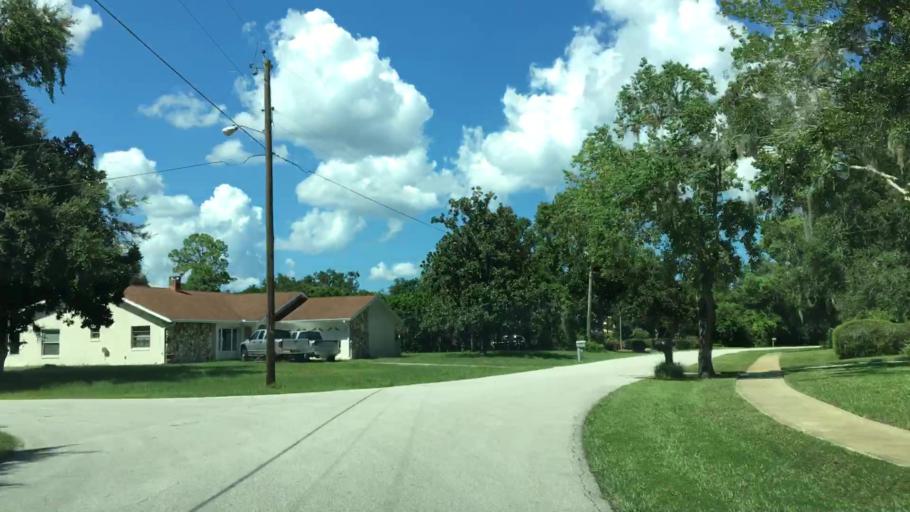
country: US
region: Florida
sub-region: Volusia County
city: Deltona
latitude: 28.8793
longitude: -81.2225
